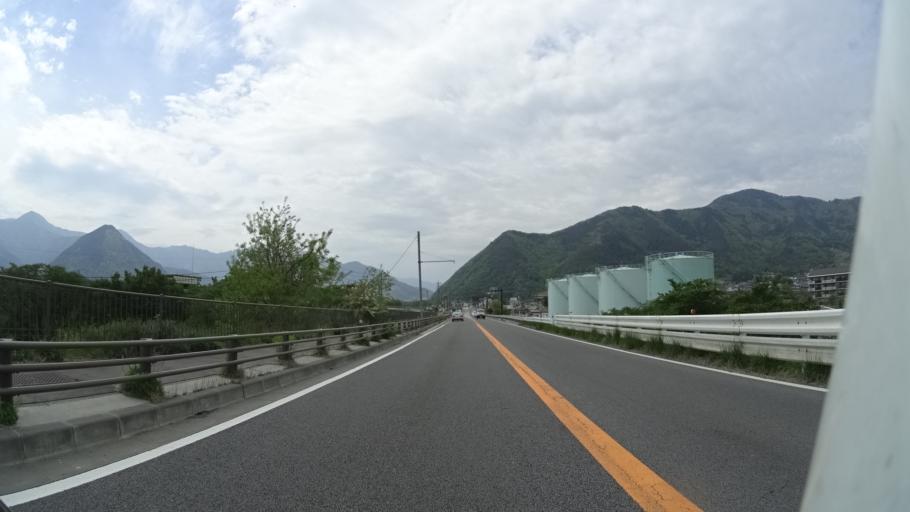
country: JP
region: Nagano
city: Ueda
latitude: 36.4577
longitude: 138.1846
